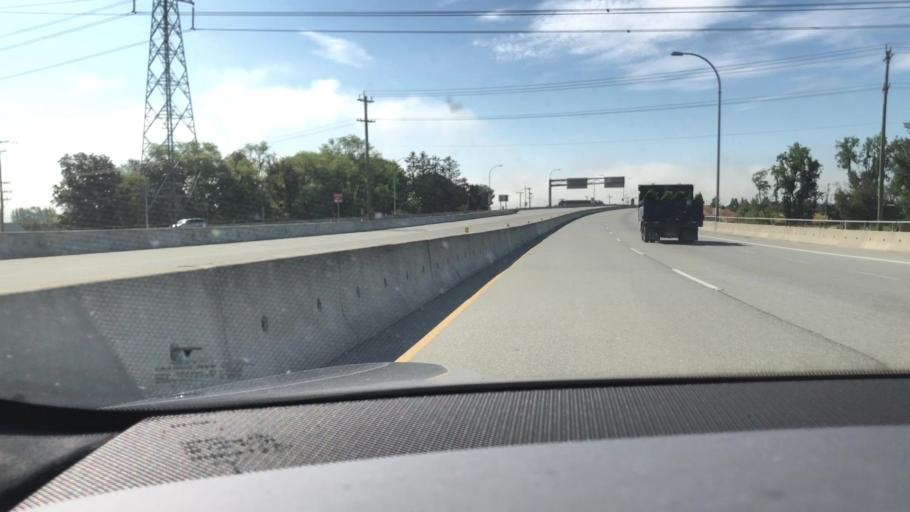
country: CA
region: British Columbia
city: Ladner
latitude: 49.0928
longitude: -123.0254
